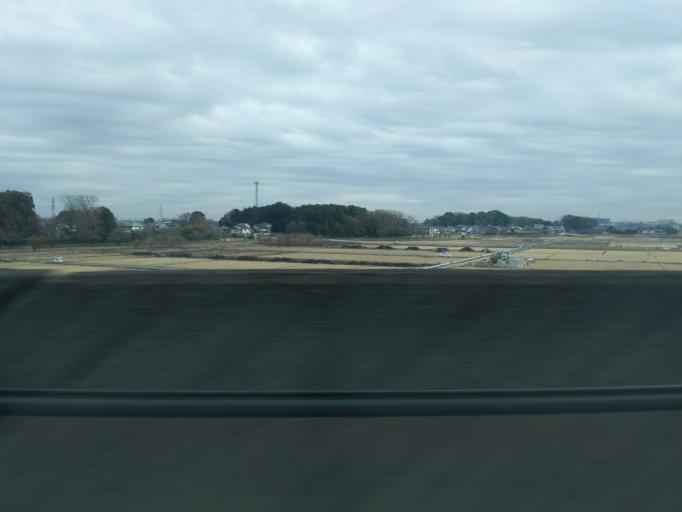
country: JP
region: Saitama
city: Shiraoka
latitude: 36.0009
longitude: 139.6399
